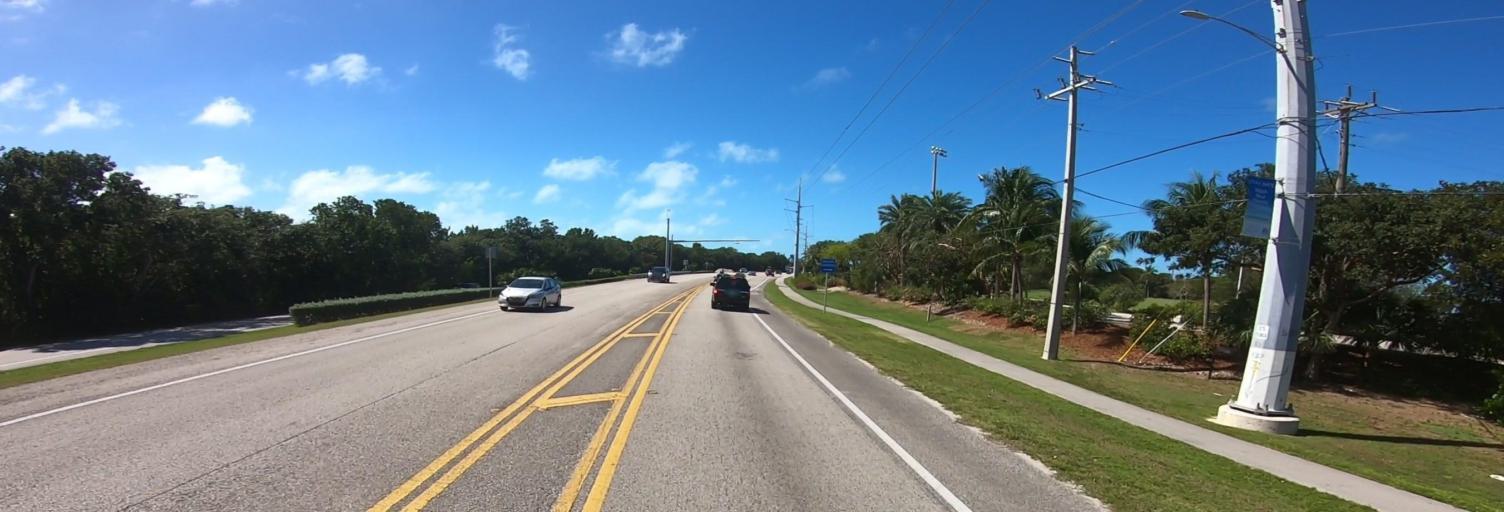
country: US
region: Florida
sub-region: Monroe County
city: Plantation
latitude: 24.9616
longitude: -80.5662
